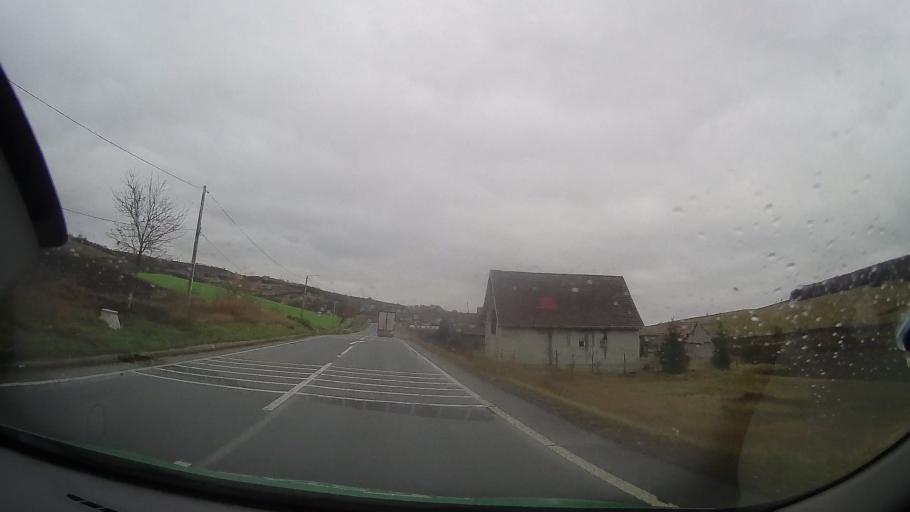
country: RO
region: Mures
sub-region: Comuna Lunca
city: Lunca
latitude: 46.8579
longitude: 24.5624
